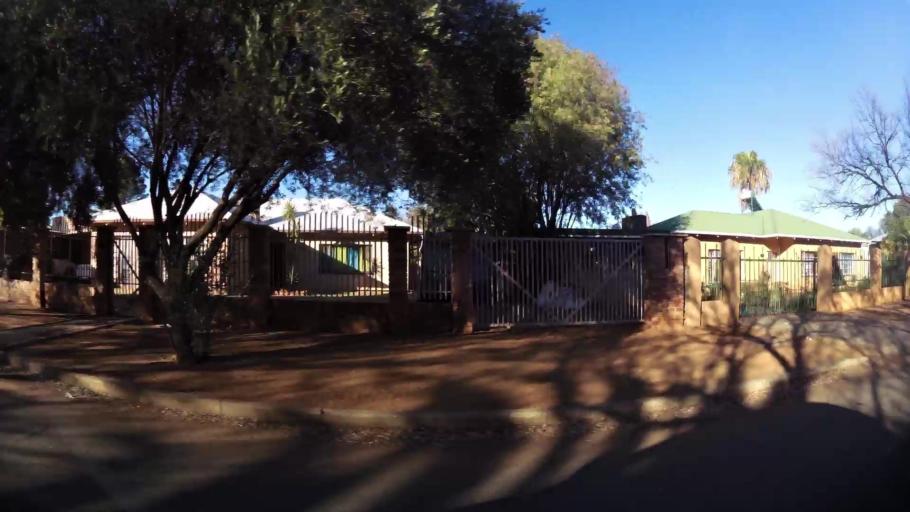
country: ZA
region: Northern Cape
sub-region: Frances Baard District Municipality
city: Kimberley
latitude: -28.7406
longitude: 24.7415
